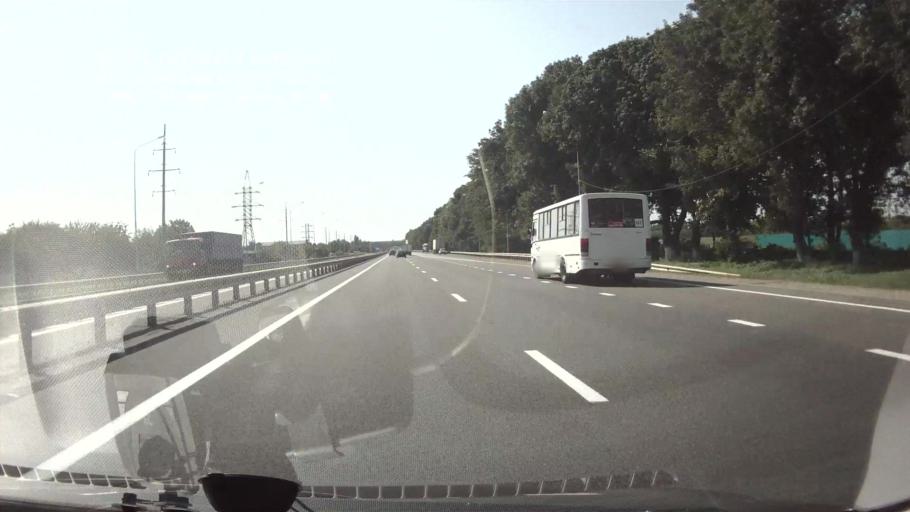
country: RU
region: Krasnodarskiy
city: Starokorsunskaya
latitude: 45.0251
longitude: 39.2133
